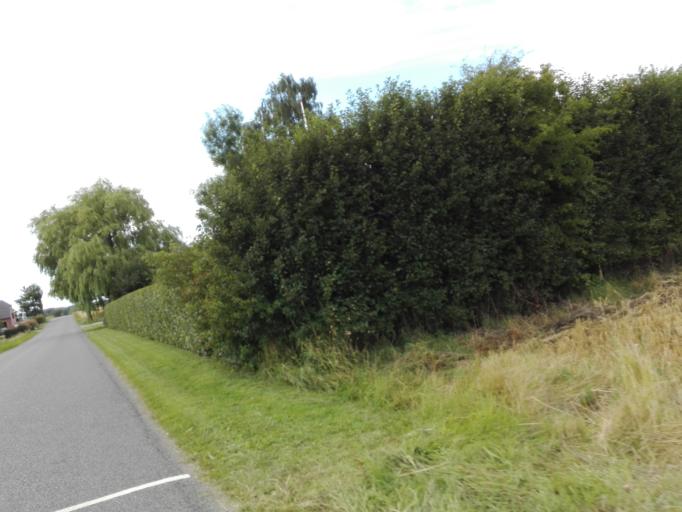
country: DK
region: Central Jutland
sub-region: Skanderborg Kommune
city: Horning
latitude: 56.0989
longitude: 10.0112
